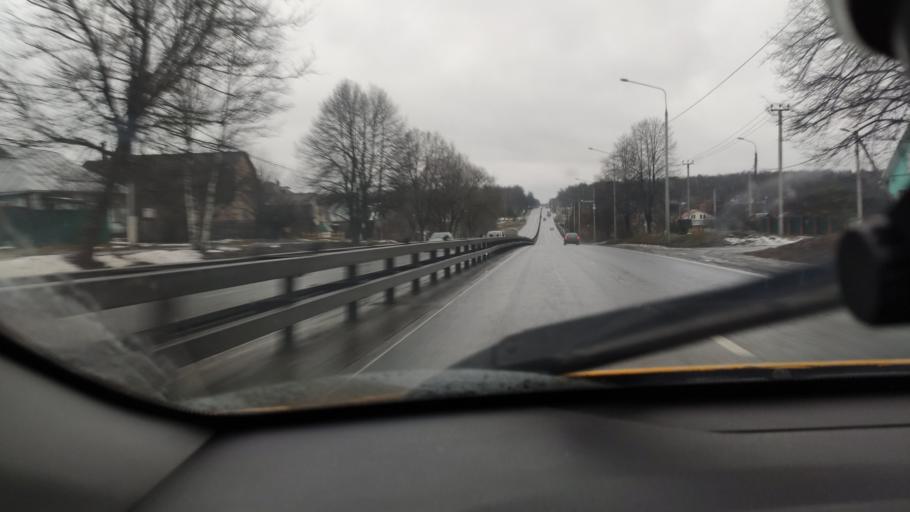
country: RU
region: Moskovskaya
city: Troitsk
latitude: 55.3232
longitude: 37.2633
